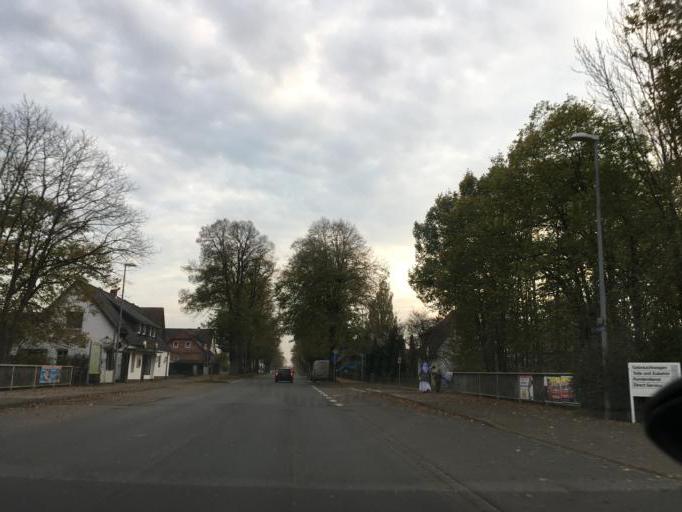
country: DE
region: Lower Saxony
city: Bergen
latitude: 52.8042
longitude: 9.9675
